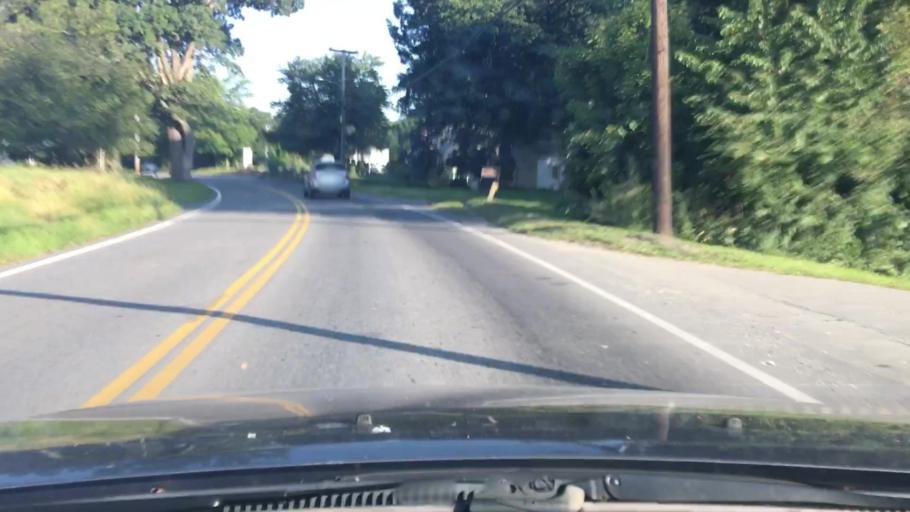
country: US
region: Massachusetts
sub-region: Worcester County
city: Westborough
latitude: 42.2559
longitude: -71.5926
